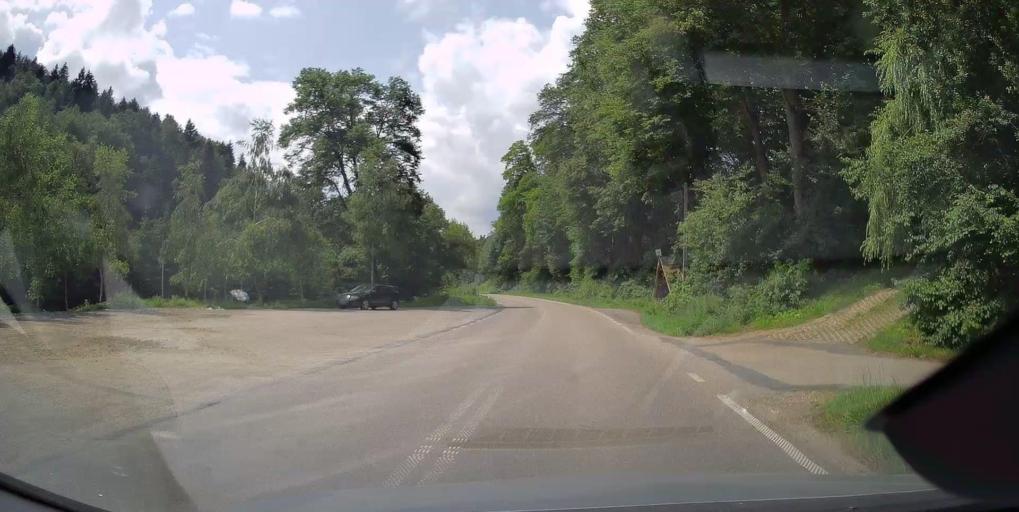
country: PL
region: Lesser Poland Voivodeship
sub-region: Powiat nowosadecki
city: Nowy Sacz
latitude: 49.6603
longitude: 20.7309
